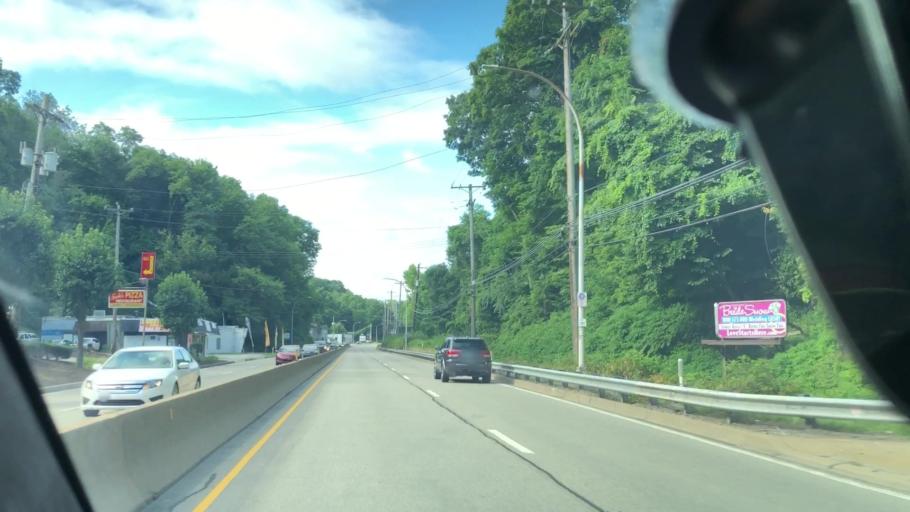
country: US
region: Pennsylvania
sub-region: Allegheny County
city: Green Tree
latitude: 40.4131
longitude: -80.0306
